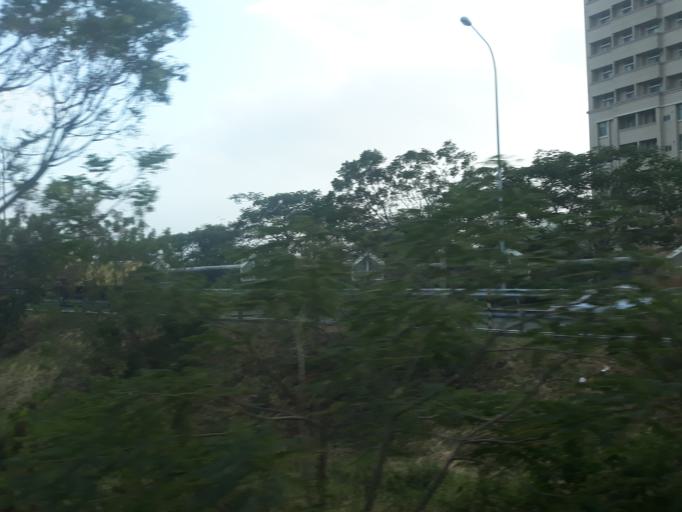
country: TW
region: Taiwan
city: Xinying
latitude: 23.1804
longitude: 120.2343
